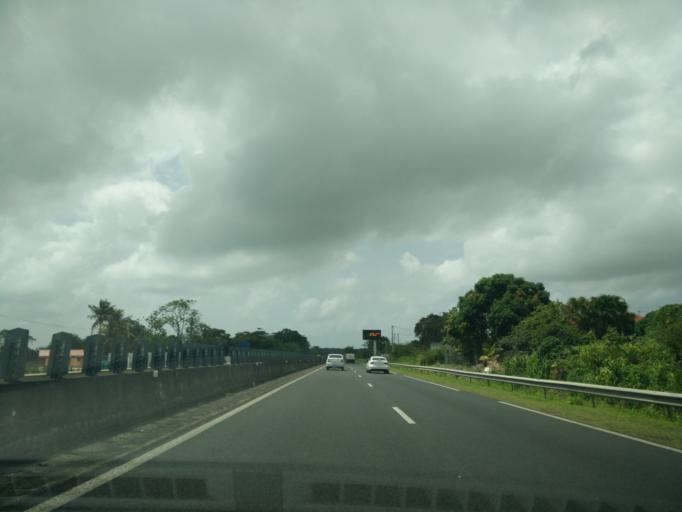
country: GP
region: Guadeloupe
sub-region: Guadeloupe
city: Petit-Bourg
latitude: 16.1782
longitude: -61.5952
